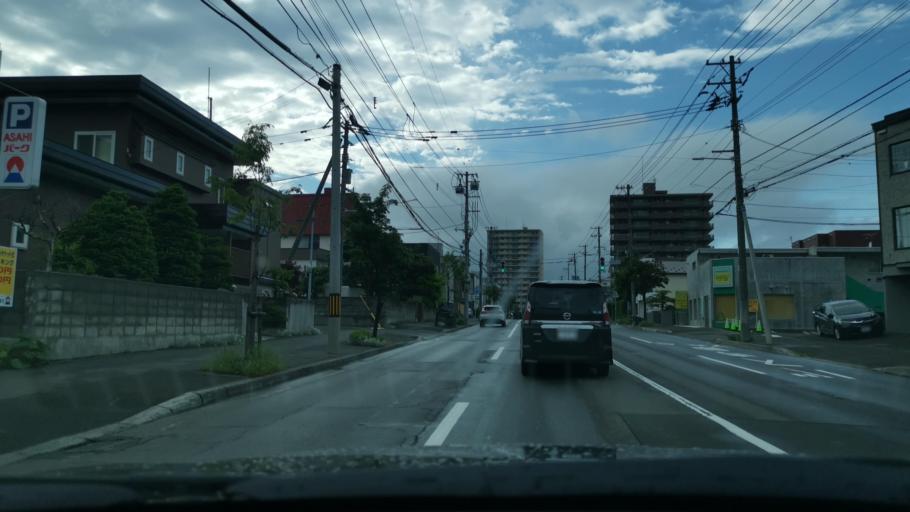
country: JP
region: Hokkaido
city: Sapporo
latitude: 43.0717
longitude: 141.2878
